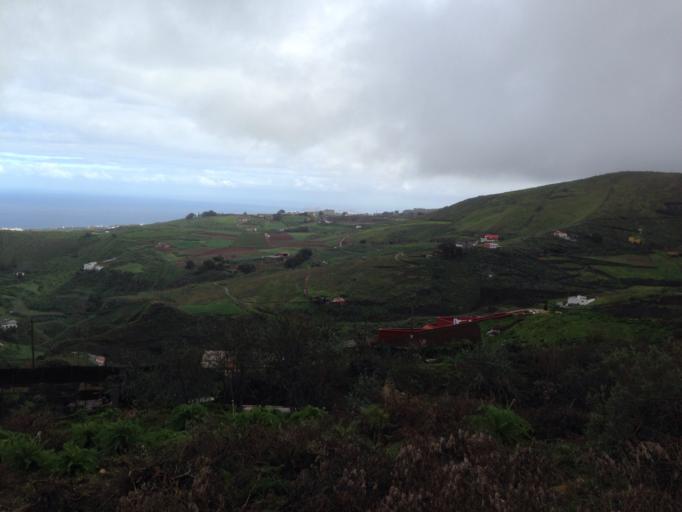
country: ES
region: Canary Islands
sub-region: Provincia de Las Palmas
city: Guia
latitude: 28.1020
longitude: -15.6399
